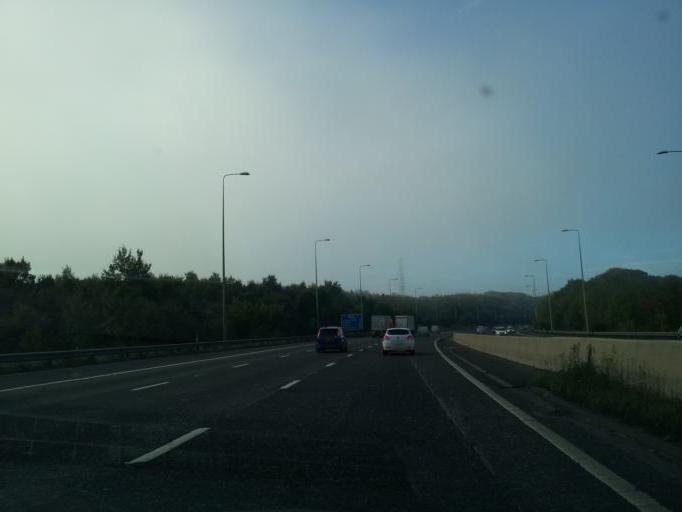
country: GB
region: England
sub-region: Calderdale
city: Brighouse
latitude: 53.6893
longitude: -1.7593
